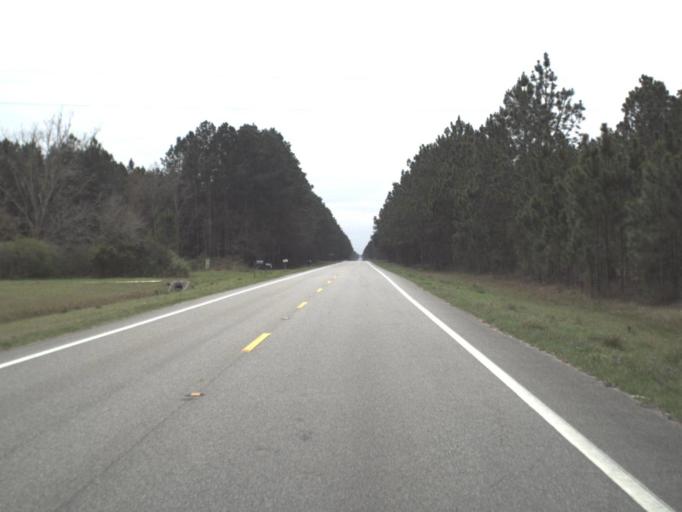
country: US
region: Florida
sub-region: Gulf County
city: Port Saint Joe
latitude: 29.9375
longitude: -85.1893
